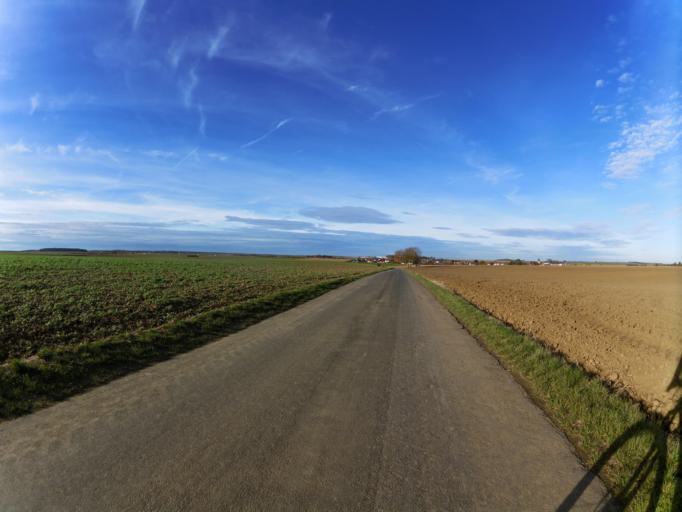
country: DE
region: Bavaria
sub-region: Regierungsbezirk Unterfranken
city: Giebelstadt
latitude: 49.6614
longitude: 9.9583
